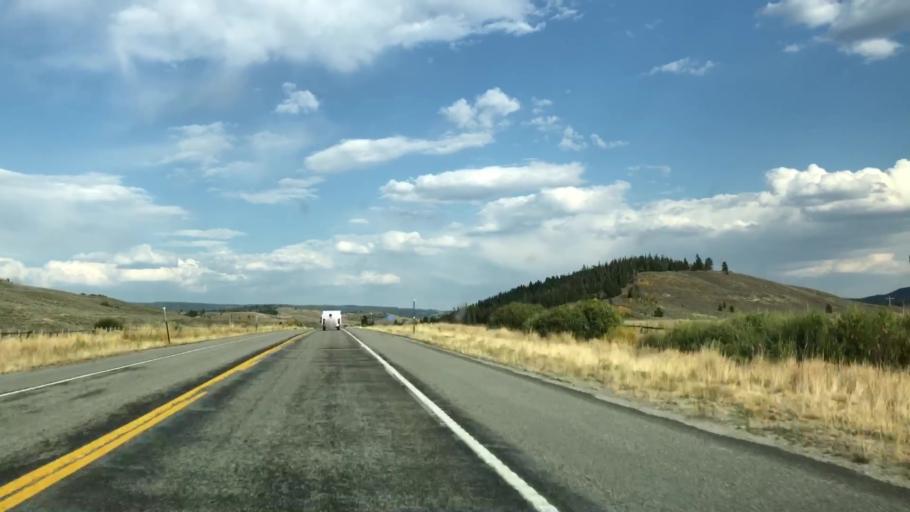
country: US
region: Wyoming
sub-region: Teton County
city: Hoback
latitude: 43.1546
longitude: -110.3309
